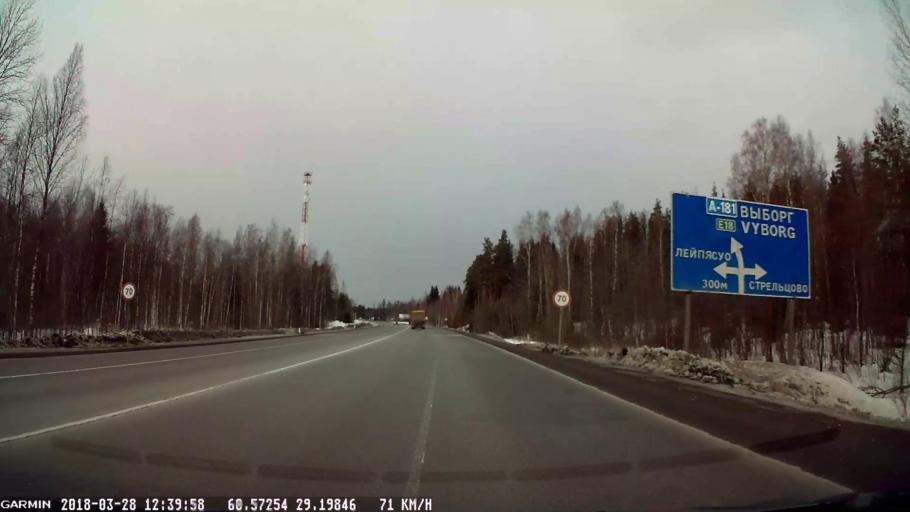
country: RU
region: Leningrad
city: Veshchevo
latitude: 60.5727
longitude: 29.1984
